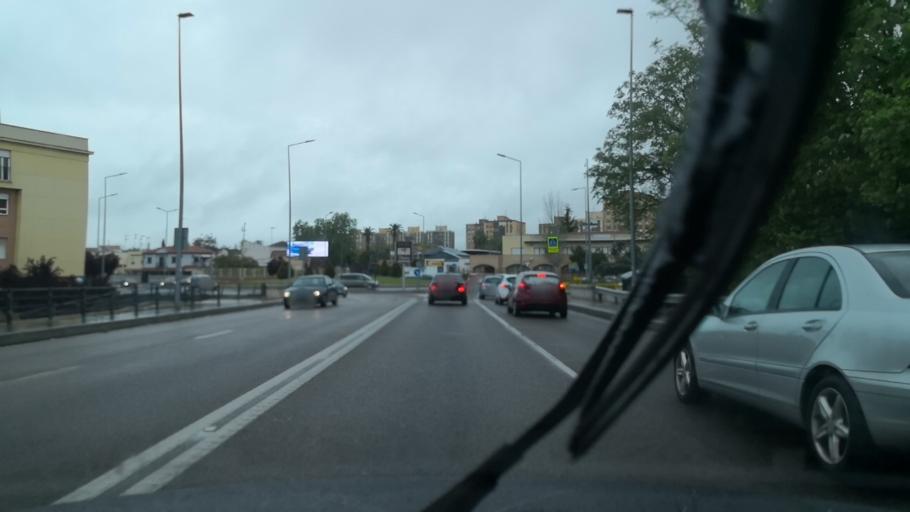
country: ES
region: Extremadura
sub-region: Provincia de Badajoz
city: Badajoz
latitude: 38.8832
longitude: -6.9847
